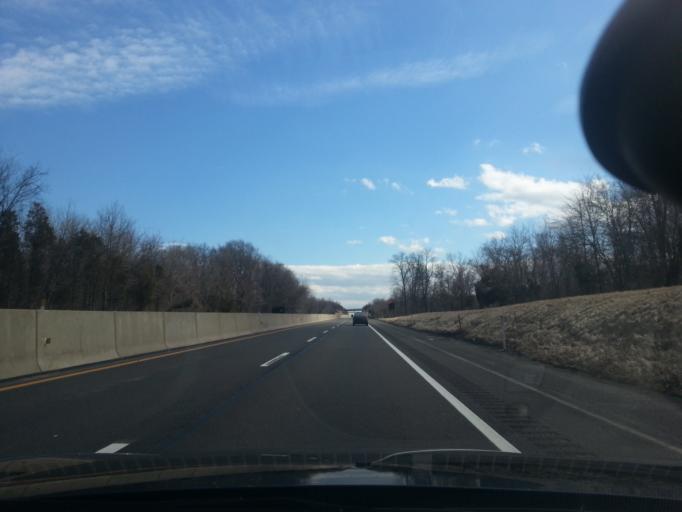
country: US
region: Pennsylvania
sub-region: Montgomery County
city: Woxall
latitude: 40.3605
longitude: -75.3963
